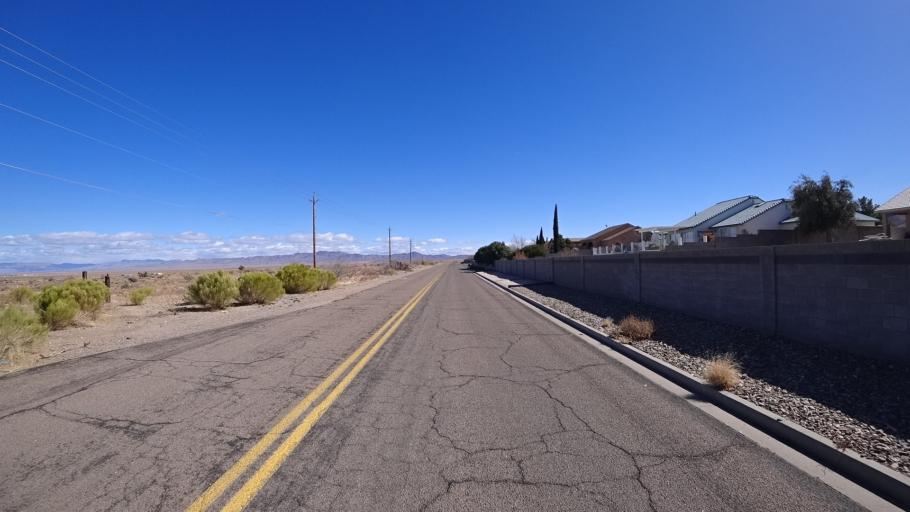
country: US
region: Arizona
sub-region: Mohave County
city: Kingman
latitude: 35.2037
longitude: -113.9674
